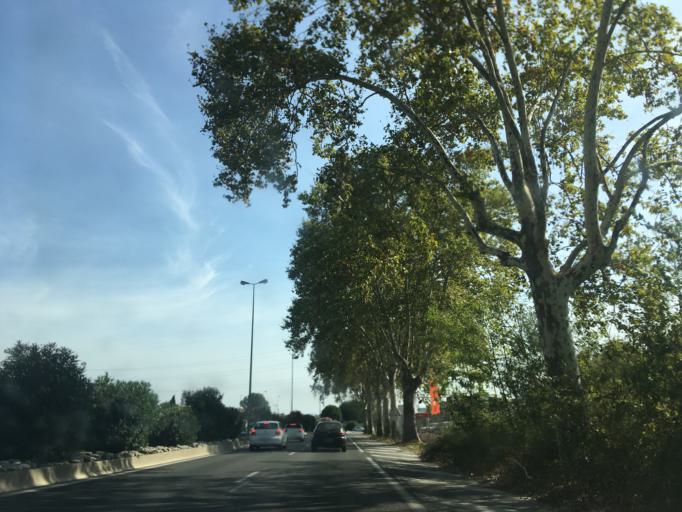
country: FR
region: Provence-Alpes-Cote d'Azur
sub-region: Departement du Var
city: Trans-en-Provence
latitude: 43.5102
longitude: 6.4802
